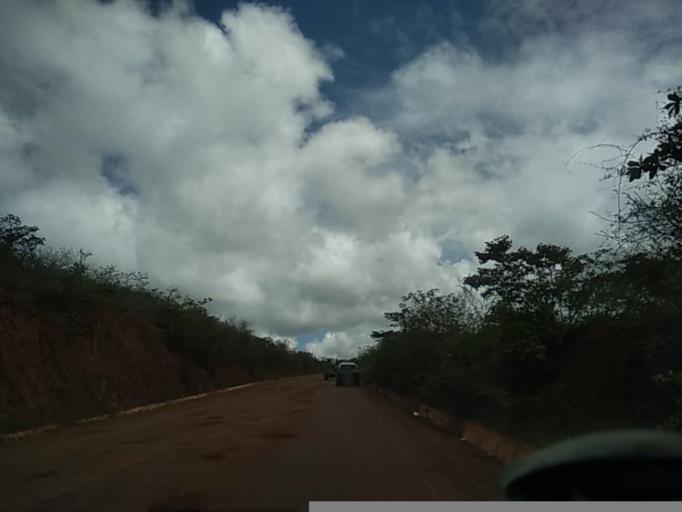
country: BR
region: Bahia
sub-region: Caetite
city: Caetite
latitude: -14.0295
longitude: -42.4876
